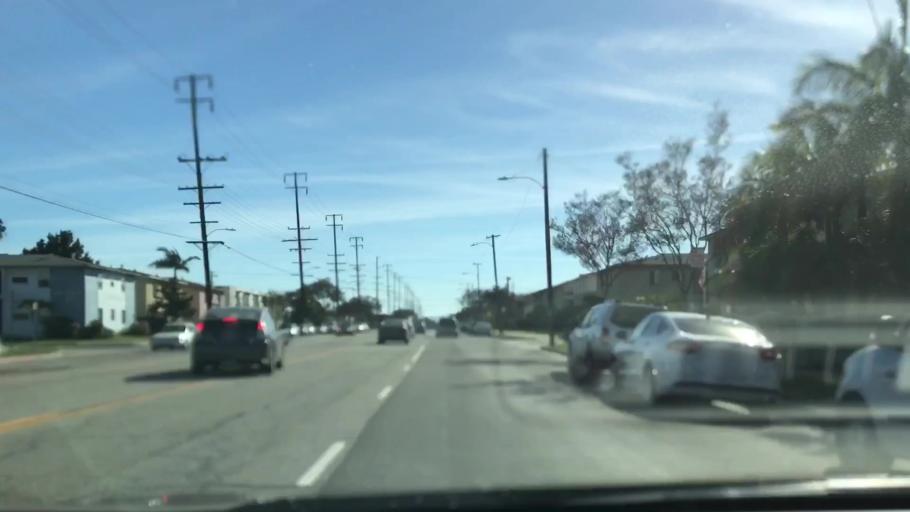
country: US
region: California
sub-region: Los Angeles County
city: Alondra Park
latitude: 33.8784
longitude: -118.3266
